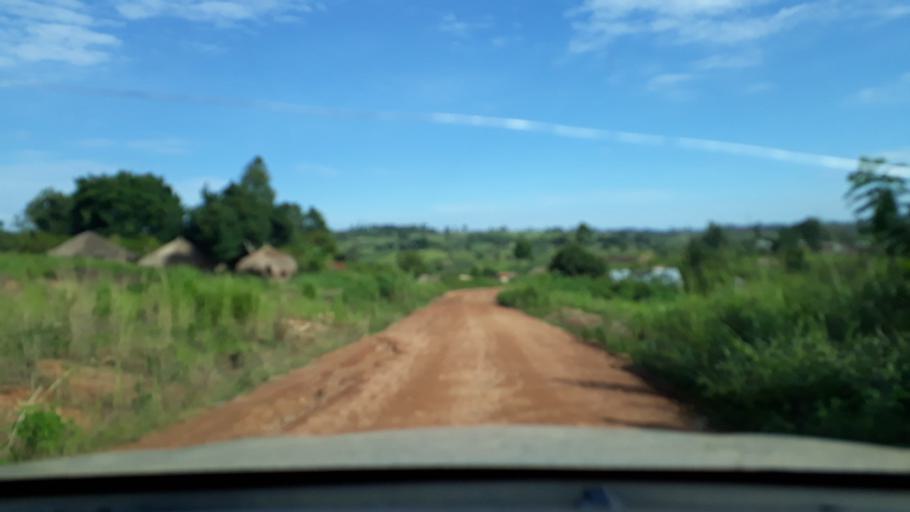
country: UG
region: Northern Region
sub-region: Zombo District
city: Paidha
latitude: 2.3658
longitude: 31.0280
